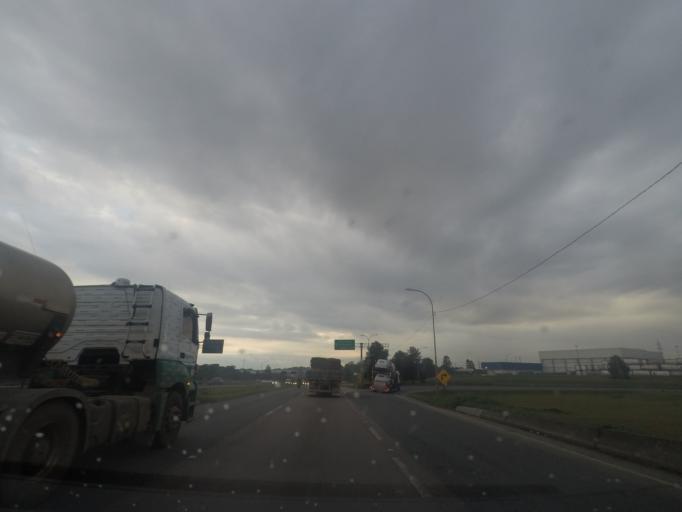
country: BR
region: Parana
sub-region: Sao Jose Dos Pinhais
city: Sao Jose dos Pinhais
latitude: -25.5690
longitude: -49.1826
